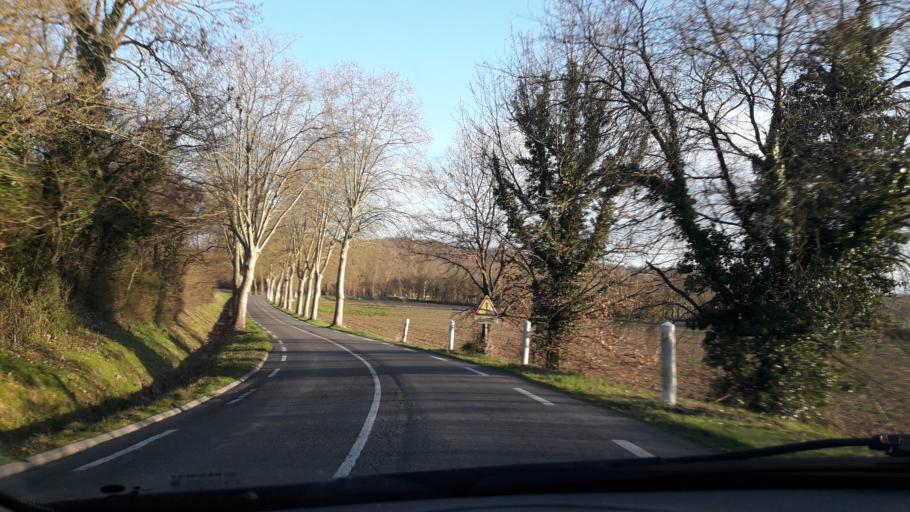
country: FR
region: Midi-Pyrenees
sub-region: Departement de la Haute-Garonne
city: Montaigut-sur-Save
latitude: 43.7220
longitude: 1.2456
